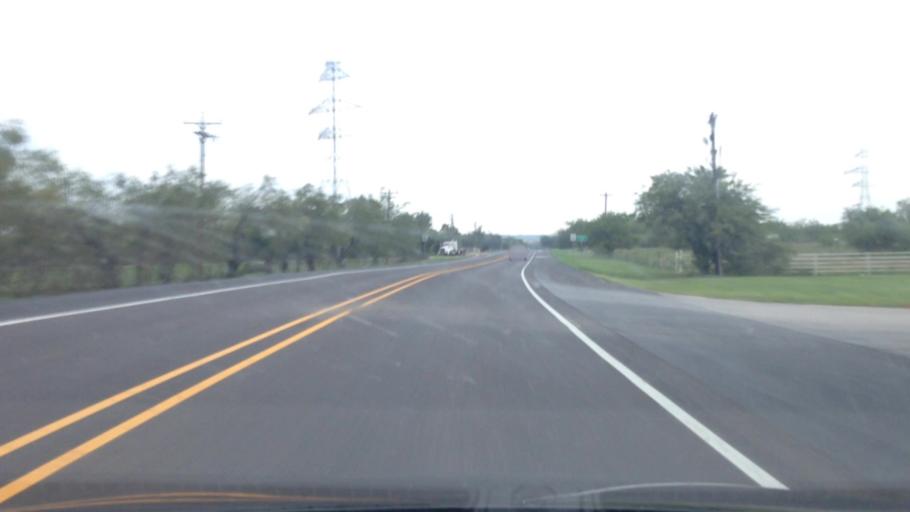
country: US
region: Texas
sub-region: Johnson County
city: Burleson
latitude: 32.5068
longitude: -97.3459
